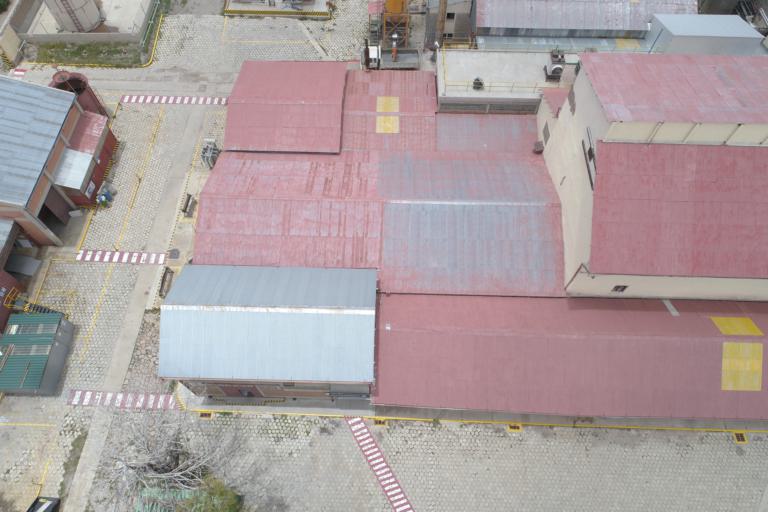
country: BO
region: Oruro
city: Challapata
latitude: -19.0110
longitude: -66.7805
